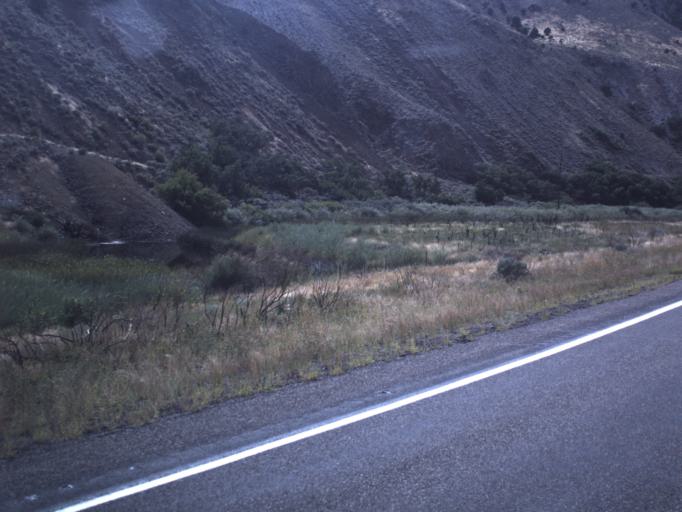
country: US
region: Utah
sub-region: Sevier County
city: Monroe
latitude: 38.4913
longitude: -112.2449
